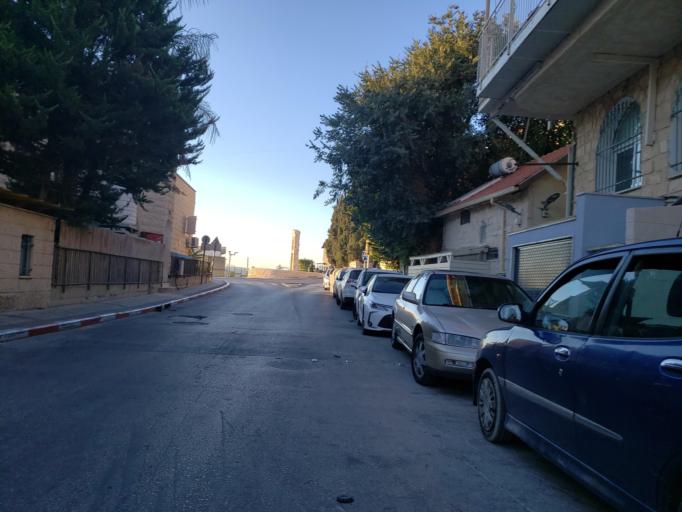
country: IL
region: Northern District
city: Safed
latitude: 32.9713
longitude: 35.4928
